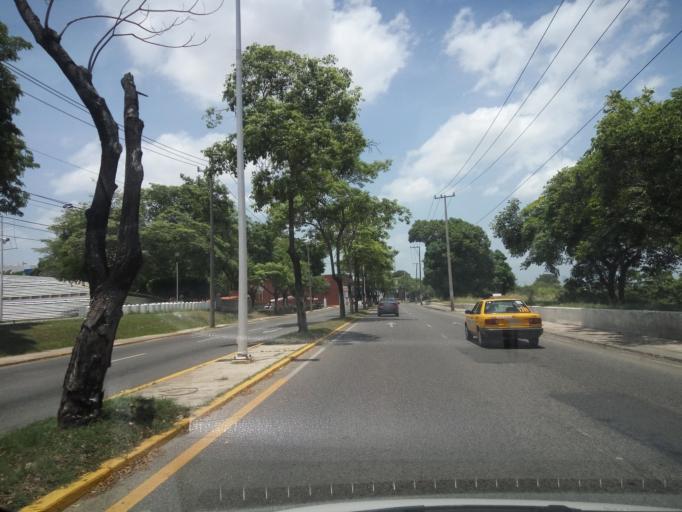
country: MX
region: Tabasco
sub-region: Nacajuca
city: Bosque de Saloya
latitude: 18.0058
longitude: -92.9543
